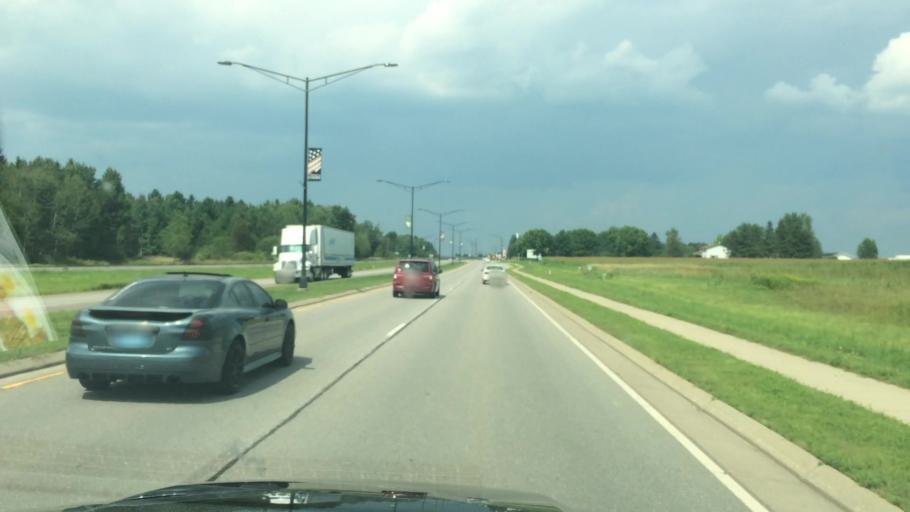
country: US
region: Wisconsin
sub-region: Clark County
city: Colby
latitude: 44.9206
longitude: -90.3157
